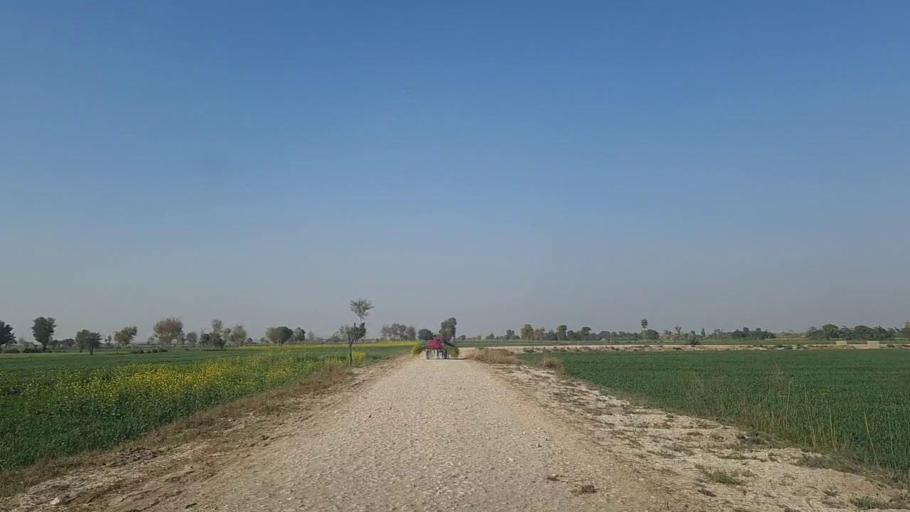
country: PK
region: Sindh
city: Jam Sahib
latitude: 26.3330
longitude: 68.7143
